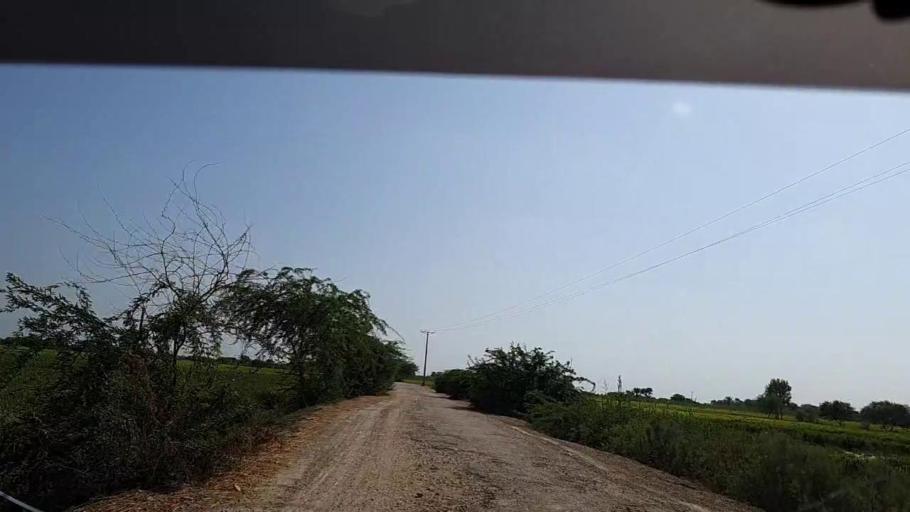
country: PK
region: Sindh
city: Badin
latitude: 24.6422
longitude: 68.7878
